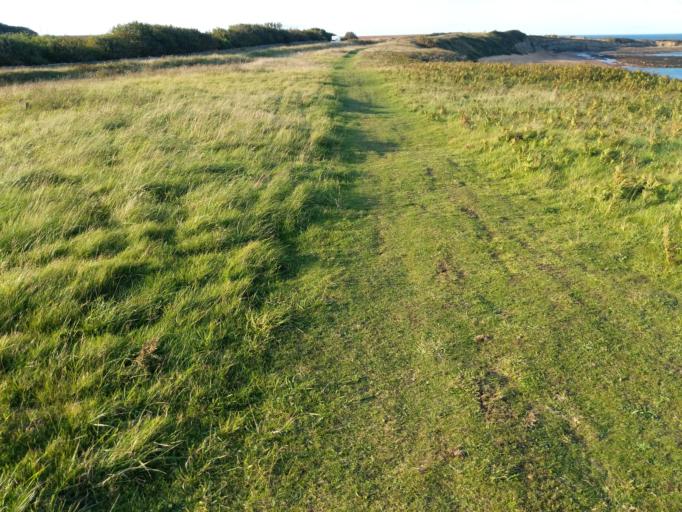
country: GB
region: England
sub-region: Northumberland
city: Lynemouth
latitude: 55.2208
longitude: -1.5297
